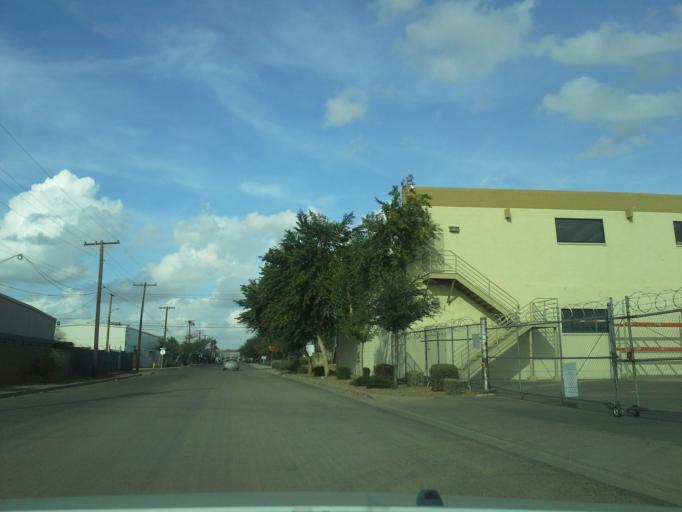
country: US
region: Arizona
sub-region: Maricopa County
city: Phoenix
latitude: 33.4250
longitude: -112.0867
